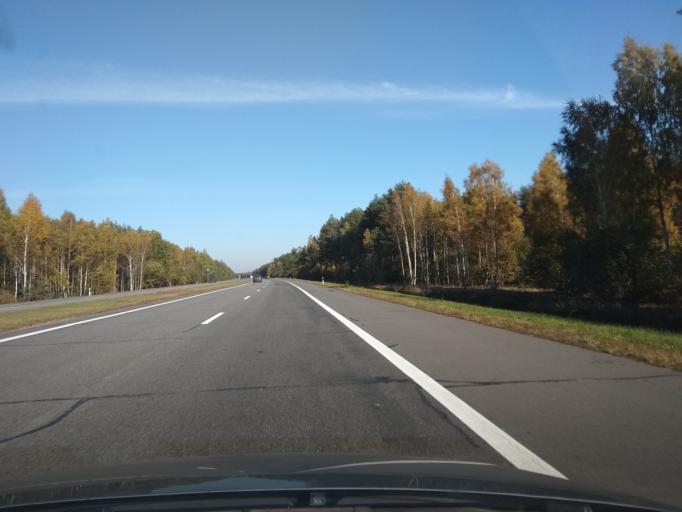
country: BY
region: Brest
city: Baranovichi
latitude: 53.0569
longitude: 25.8628
